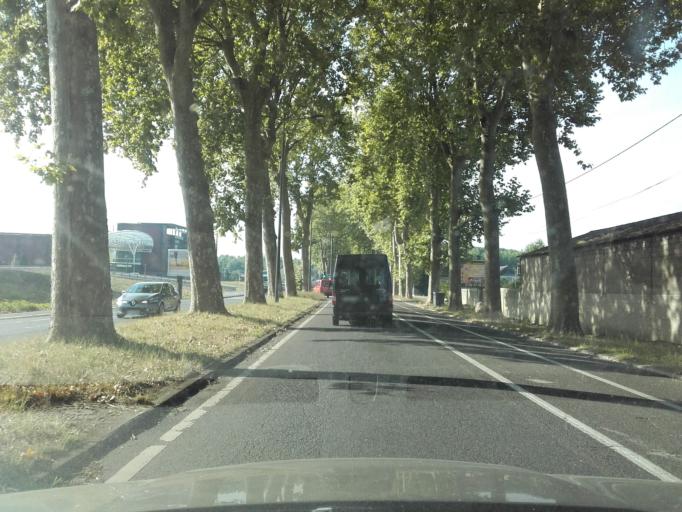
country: FR
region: Centre
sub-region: Departement d'Indre-et-Loire
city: Tours
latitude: 47.3686
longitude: 0.6763
